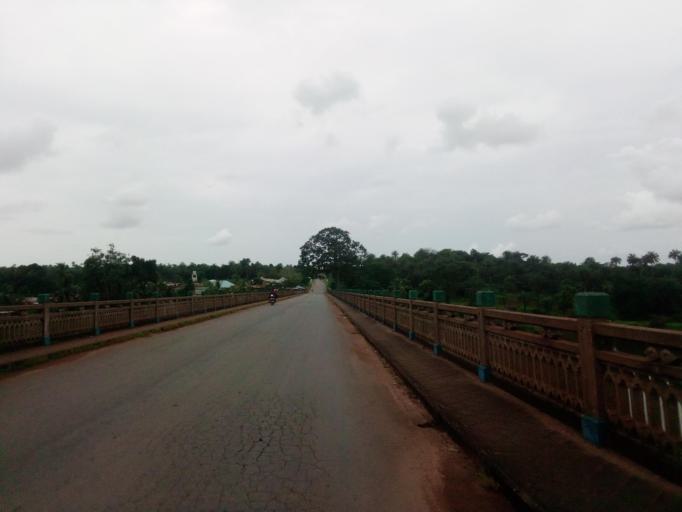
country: SL
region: Northern Province
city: Kambia
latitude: 9.1187
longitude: -12.9313
